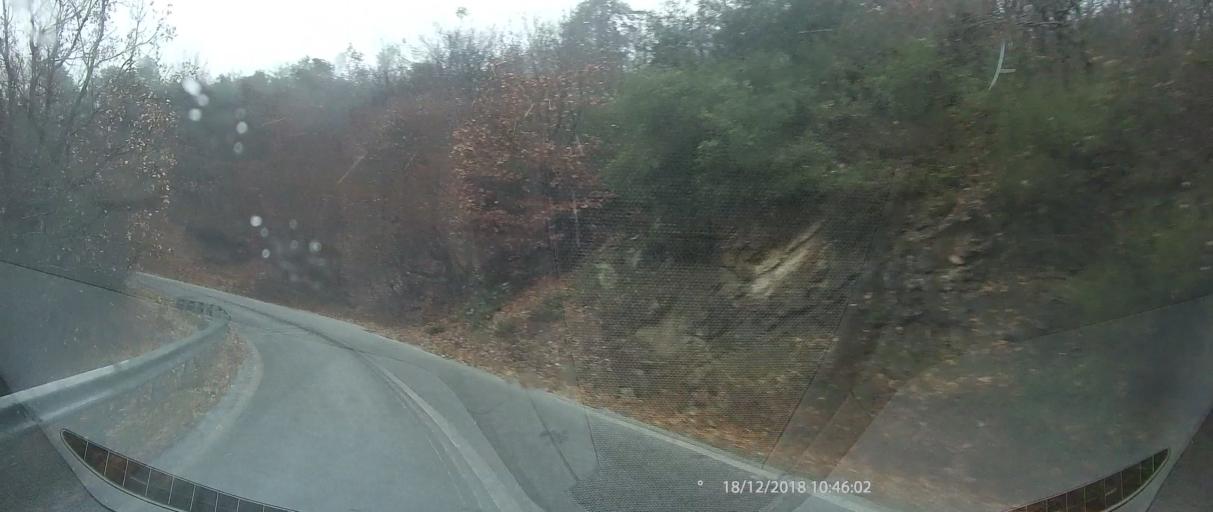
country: GR
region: Central Macedonia
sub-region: Nomos Pierias
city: Kato Milia
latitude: 40.1893
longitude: 22.3241
